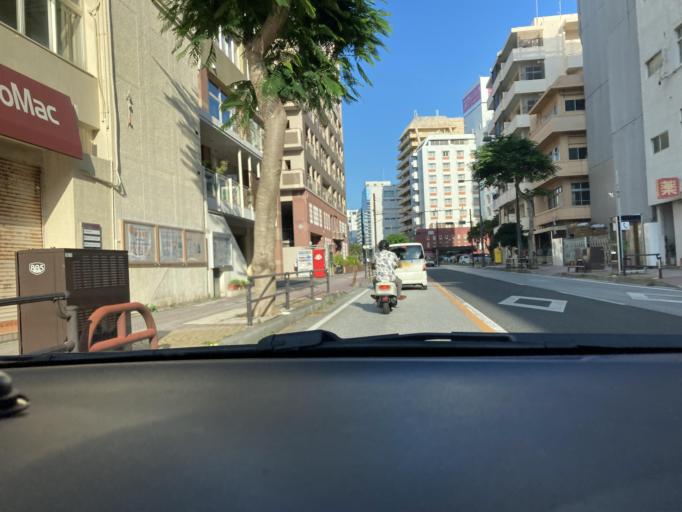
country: JP
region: Okinawa
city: Naha-shi
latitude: 26.2120
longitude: 127.6735
